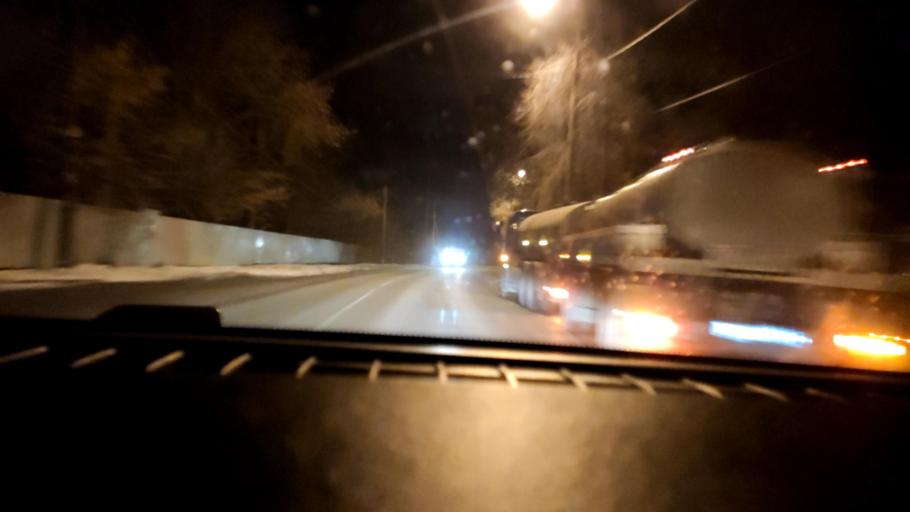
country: RU
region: Samara
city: Samara
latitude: 53.1385
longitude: 50.1498
